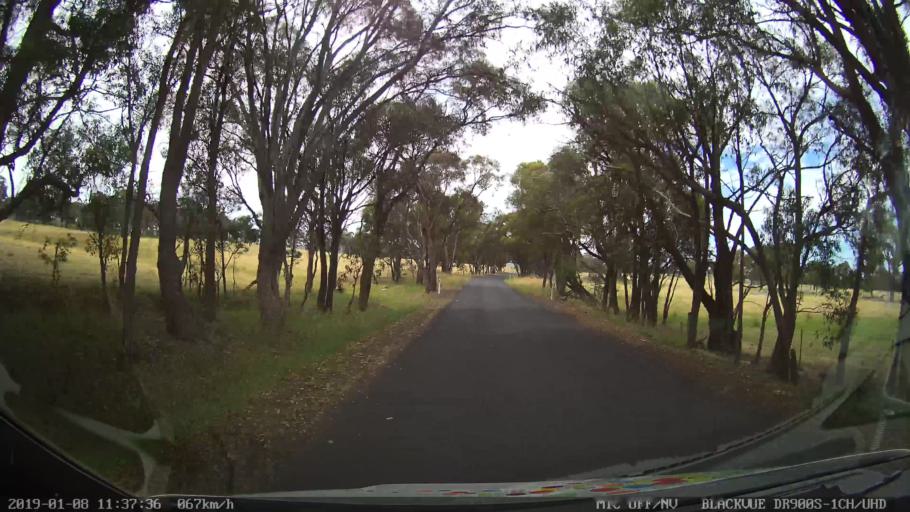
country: AU
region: New South Wales
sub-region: Guyra
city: Guyra
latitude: -30.3534
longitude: 151.5527
